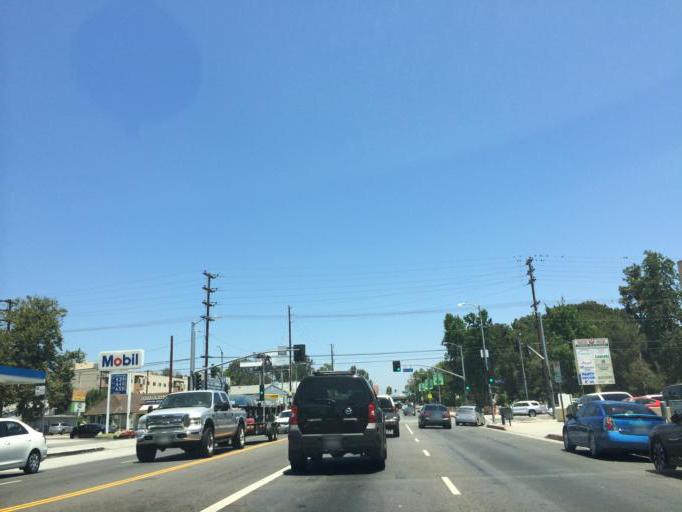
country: US
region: California
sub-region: Los Angeles County
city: North Hollywood
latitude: 34.1497
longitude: -118.3965
